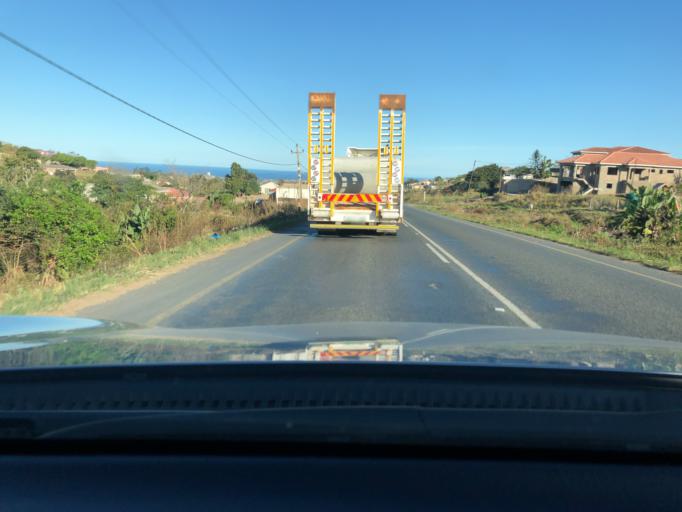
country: ZA
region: KwaZulu-Natal
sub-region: eThekwini Metropolitan Municipality
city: Umkomaas
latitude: -30.0117
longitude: 30.8056
